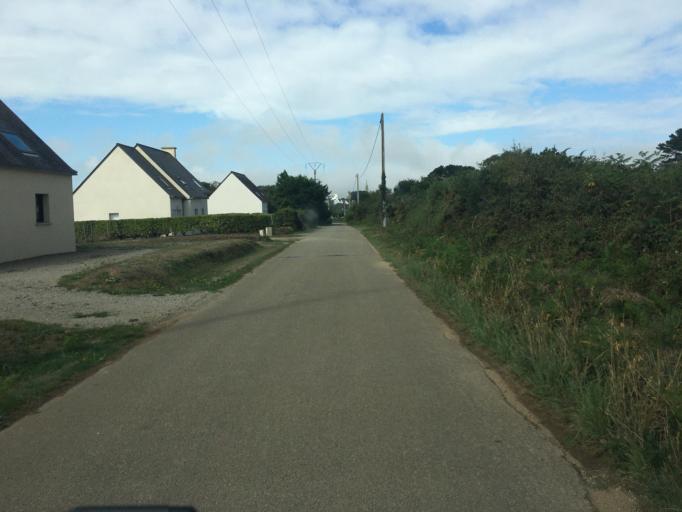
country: FR
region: Brittany
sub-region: Departement du Finistere
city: Beuzec-Cap-Sizun
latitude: 48.0750
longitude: -4.4992
